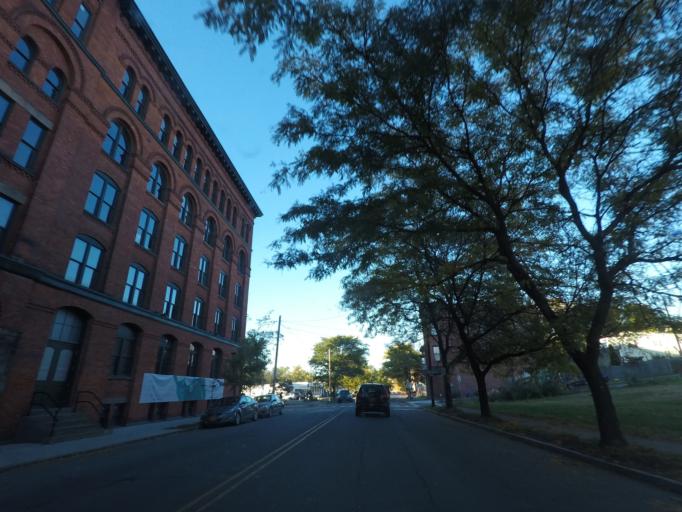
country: US
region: New York
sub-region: Albany County
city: Green Island
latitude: 42.7428
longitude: -73.6851
